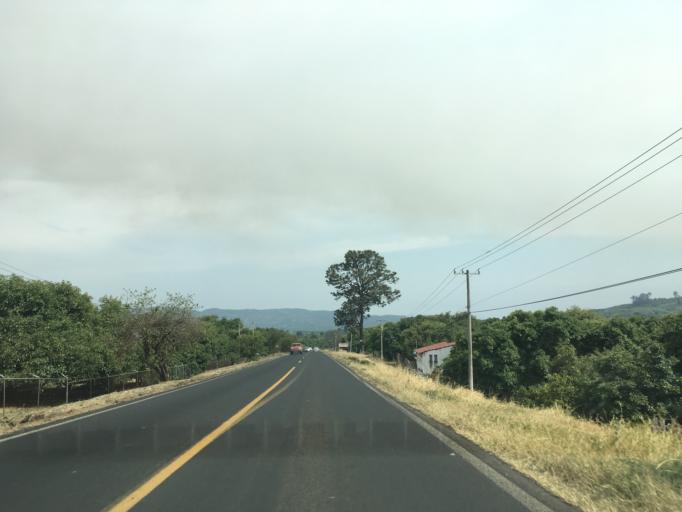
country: MX
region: Michoacan
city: Nuevo San Juan Parangaricutiro
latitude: 19.4000
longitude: -102.1083
